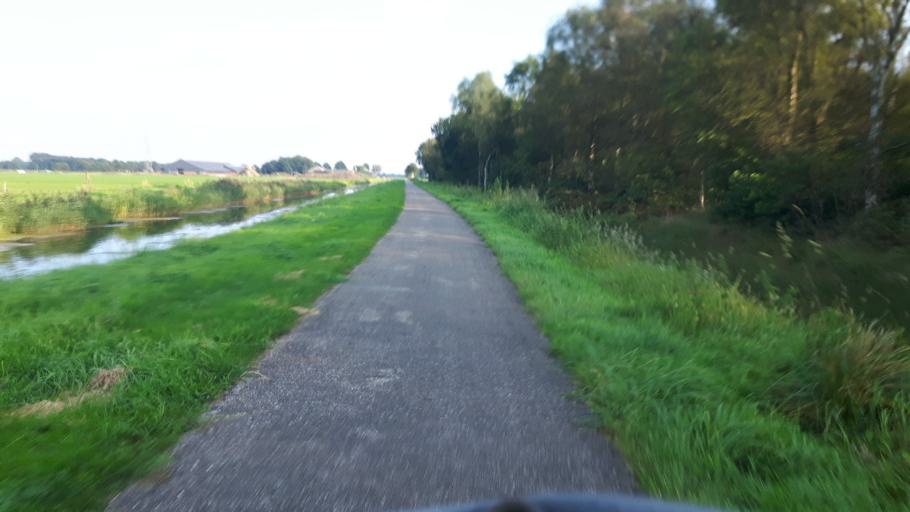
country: NL
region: Drenthe
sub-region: Gemeente Tynaarlo
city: Vries
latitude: 53.1216
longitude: 6.4998
